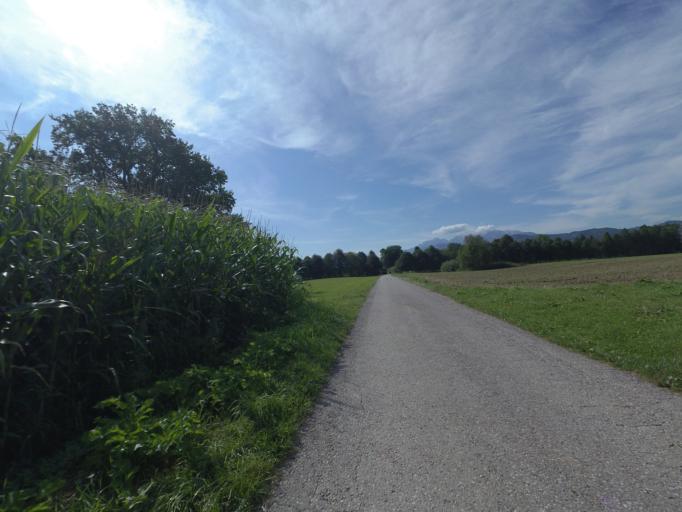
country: AT
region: Salzburg
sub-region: Politischer Bezirk Salzburg-Umgebung
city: Anif
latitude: 47.7486
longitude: 13.0730
